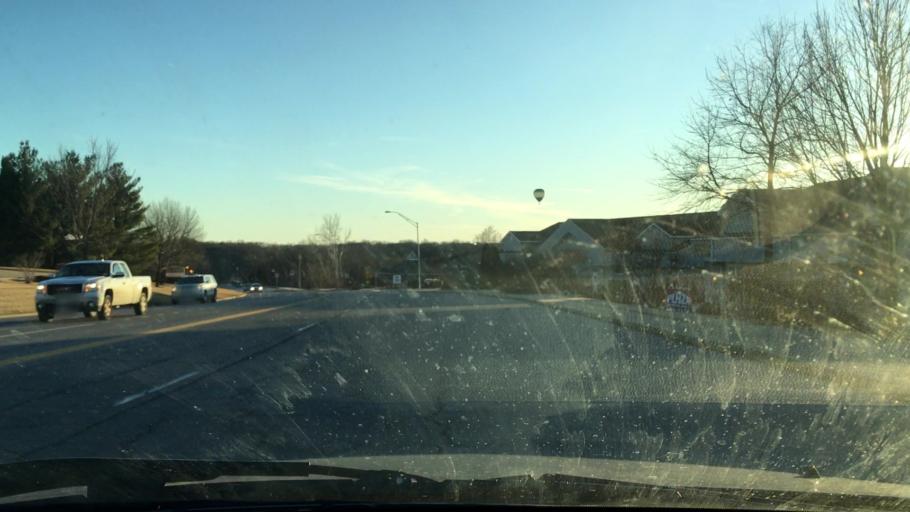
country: US
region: Missouri
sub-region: Boone County
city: Columbia
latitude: 38.9297
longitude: -92.3633
